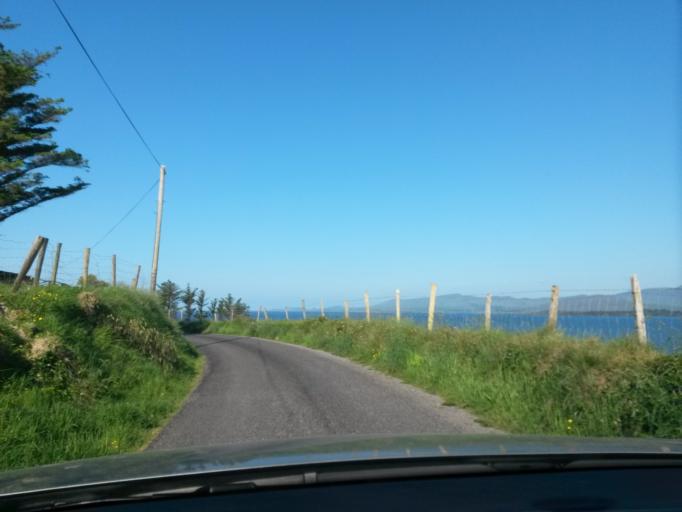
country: IE
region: Munster
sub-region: Ciarrai
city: Kenmare
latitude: 51.7909
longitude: -9.8104
